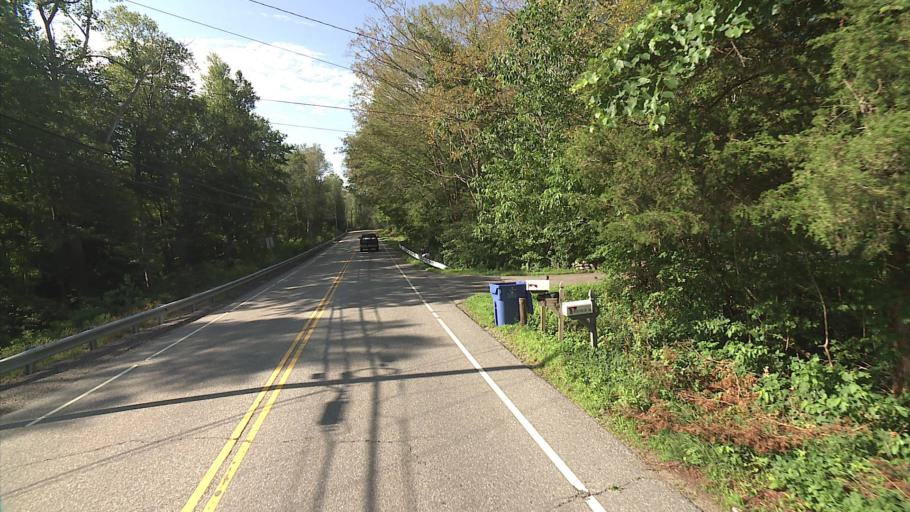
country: US
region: Connecticut
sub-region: New London County
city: Montville Center
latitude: 41.5060
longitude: -72.2032
